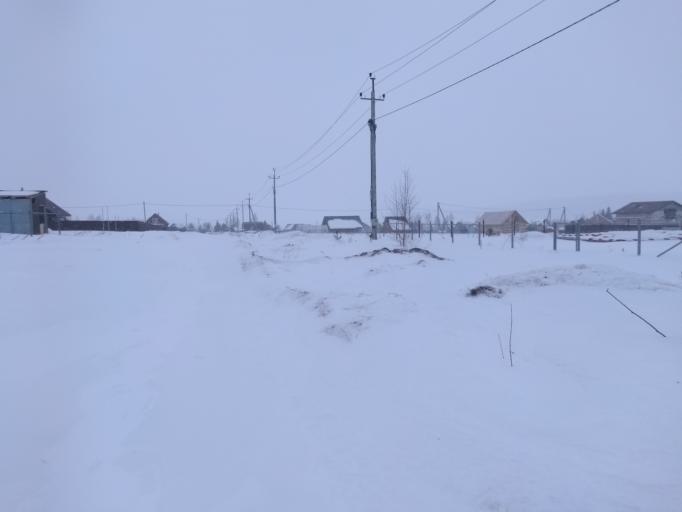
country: RU
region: Perm
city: Sylva
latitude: 57.8471
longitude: 56.7833
